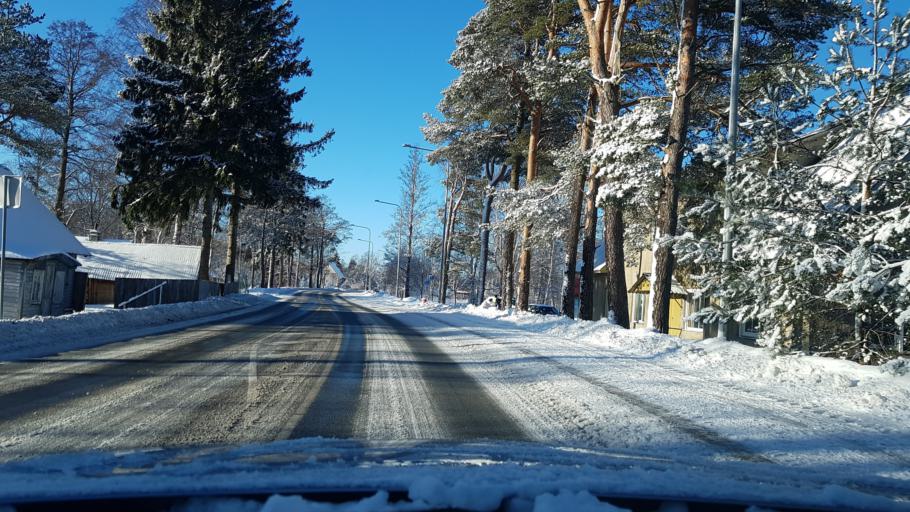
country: EE
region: Hiiumaa
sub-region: Kaerdla linn
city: Kardla
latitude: 58.9941
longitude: 22.7439
